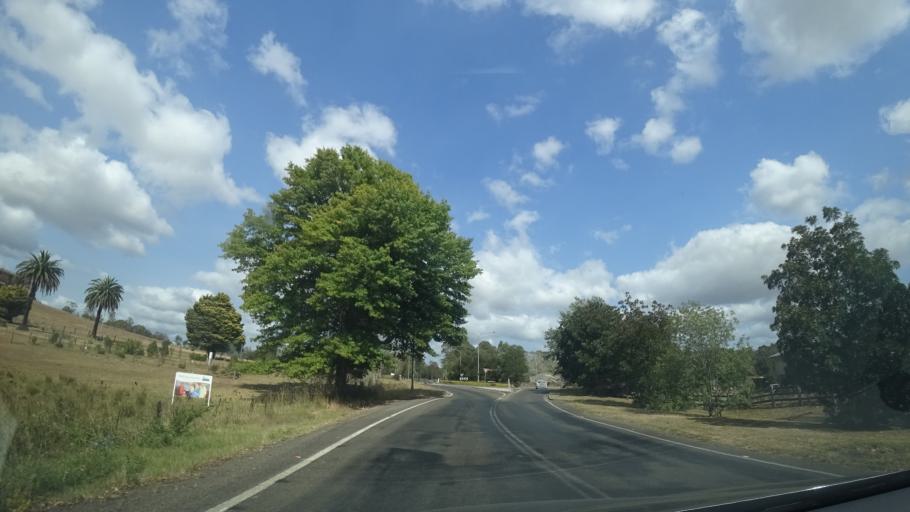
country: AU
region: New South Wales
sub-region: Wollondilly
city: Picton
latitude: -34.1858
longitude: 150.5877
